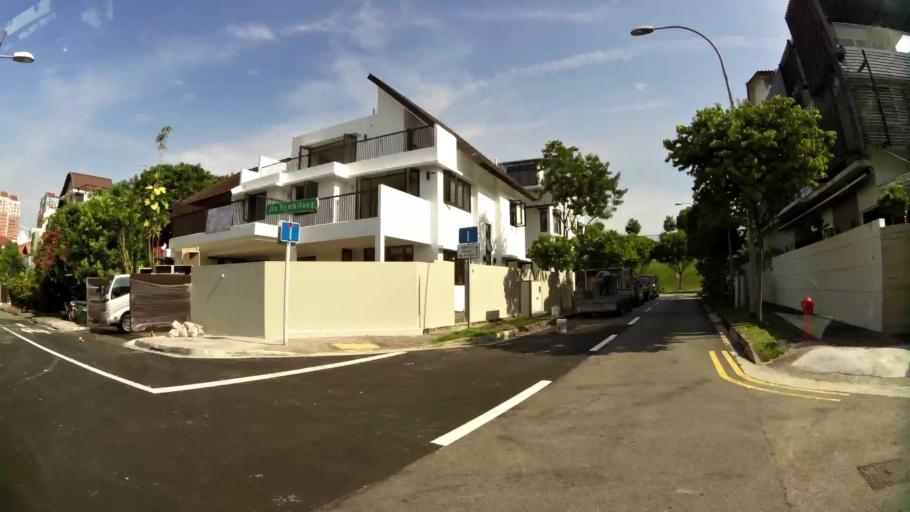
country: SG
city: Singapore
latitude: 1.3560
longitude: 103.8350
